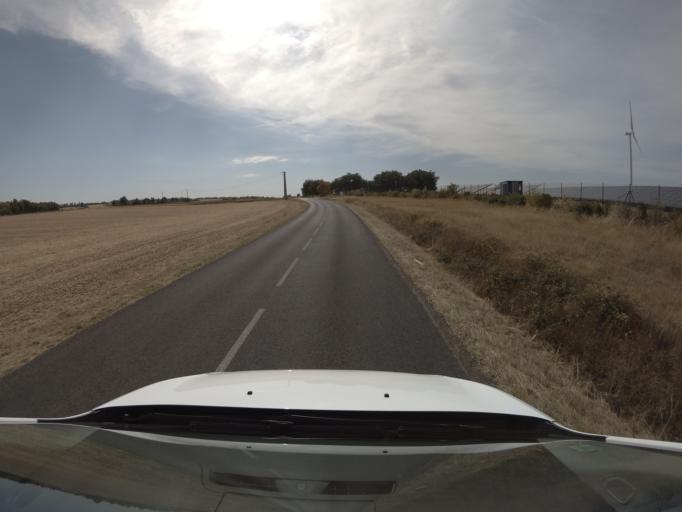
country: FR
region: Poitou-Charentes
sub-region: Departement des Deux-Sevres
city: Louzy
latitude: 46.9852
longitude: -0.1728
